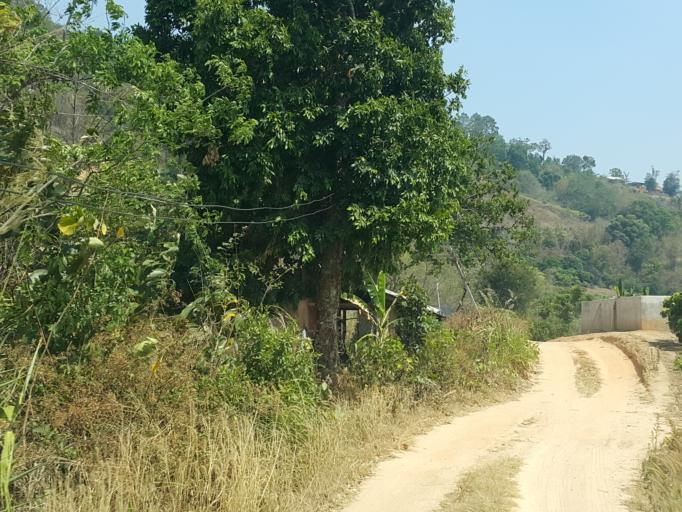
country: TH
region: Chiang Mai
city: Samoeng
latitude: 18.8885
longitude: 98.7792
